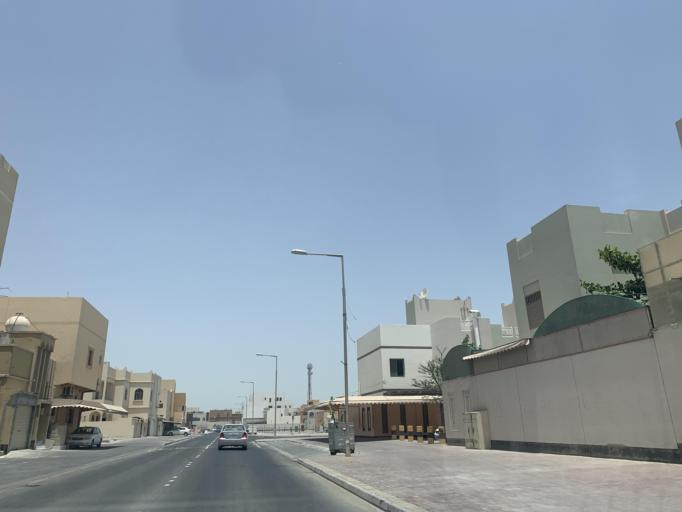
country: BH
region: Northern
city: Sitrah
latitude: 26.1603
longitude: 50.6230
